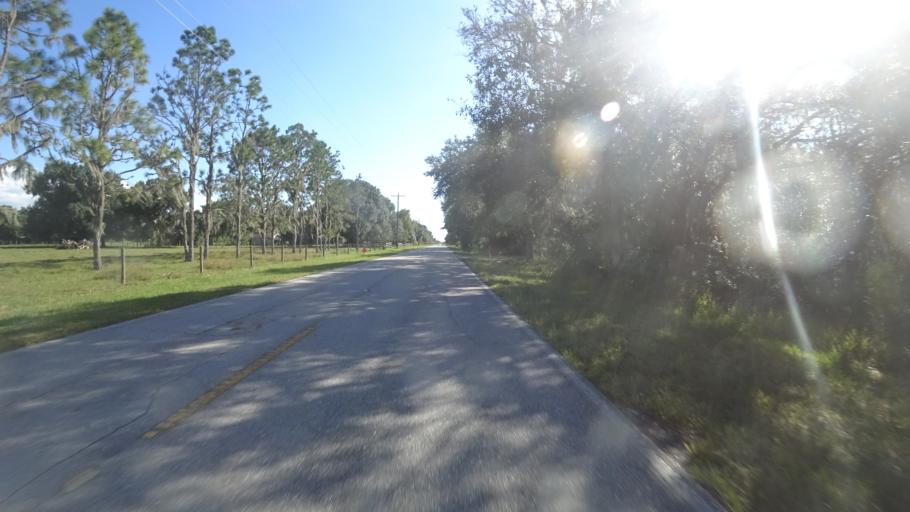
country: US
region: Florida
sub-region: Sarasota County
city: Fruitville
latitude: 27.4142
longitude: -82.2709
